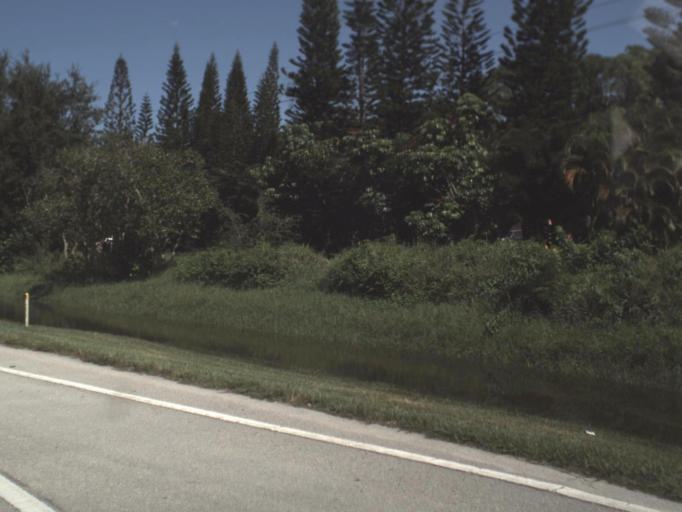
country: US
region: Florida
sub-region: Collier County
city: Pine Ridge
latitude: 26.2206
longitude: -81.8005
